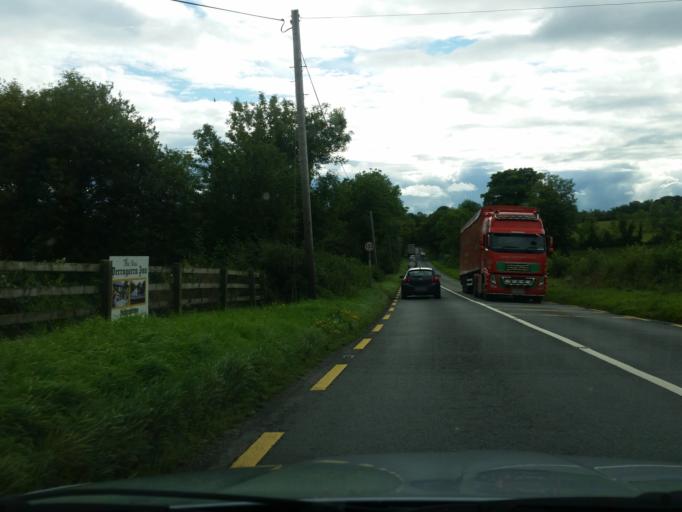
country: IE
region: Ulster
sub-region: An Cabhan
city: Belturbet
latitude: 54.1002
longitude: -7.3661
